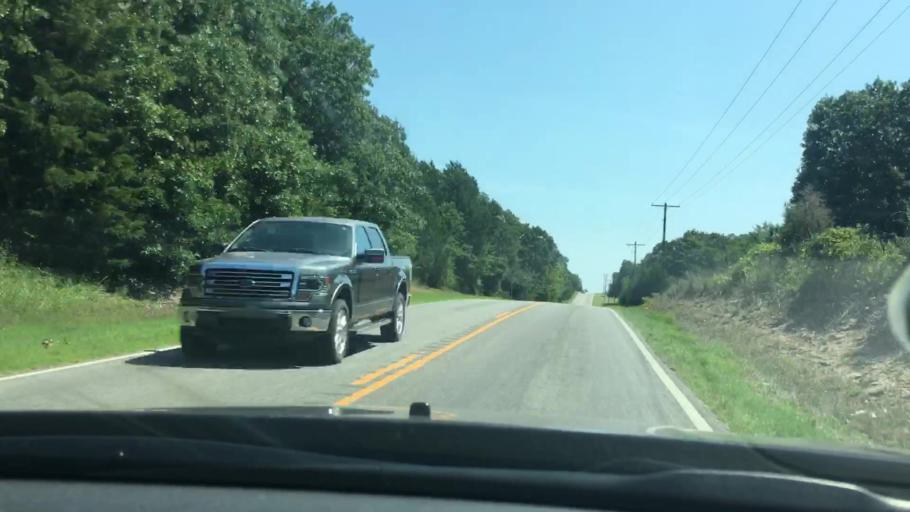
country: US
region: Oklahoma
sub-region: Johnston County
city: Tishomingo
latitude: 34.2377
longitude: -96.5869
